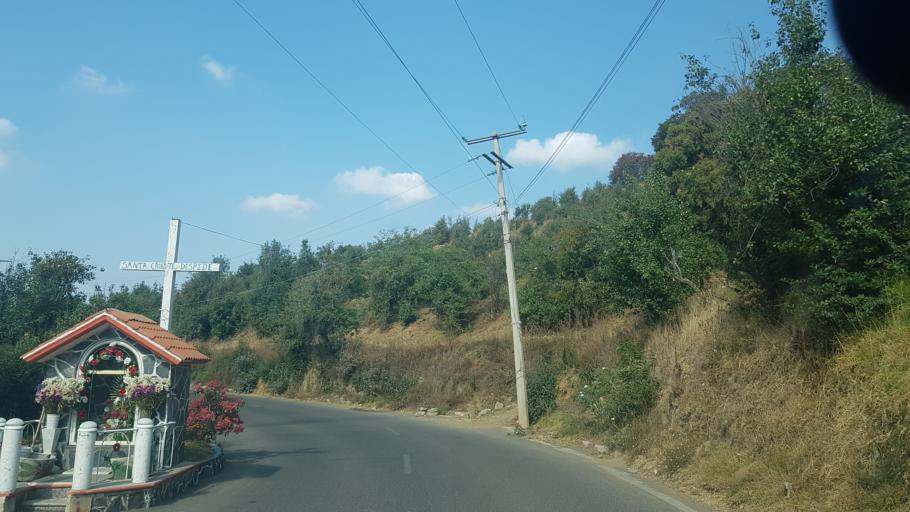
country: MX
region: Puebla
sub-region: Tochimilco
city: Santa Cruz Cuautomatitla
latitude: 18.8879
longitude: -98.6620
